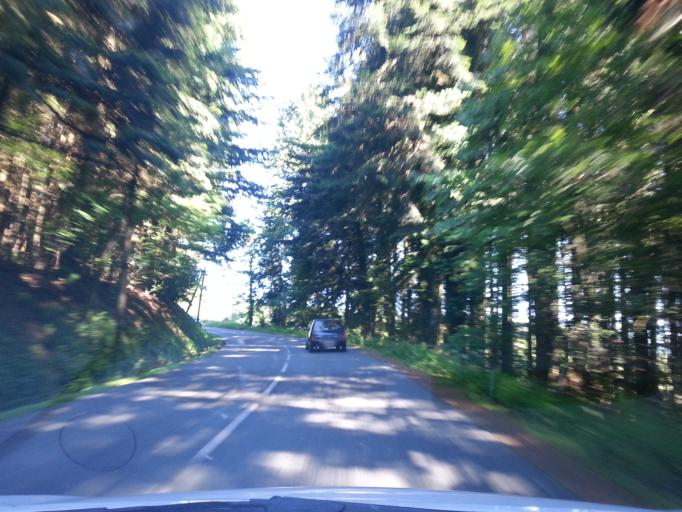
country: FR
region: Rhone-Alpes
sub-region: Departement de la Loire
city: Belmont-de-la-Loire
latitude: 46.1720
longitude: 4.4263
